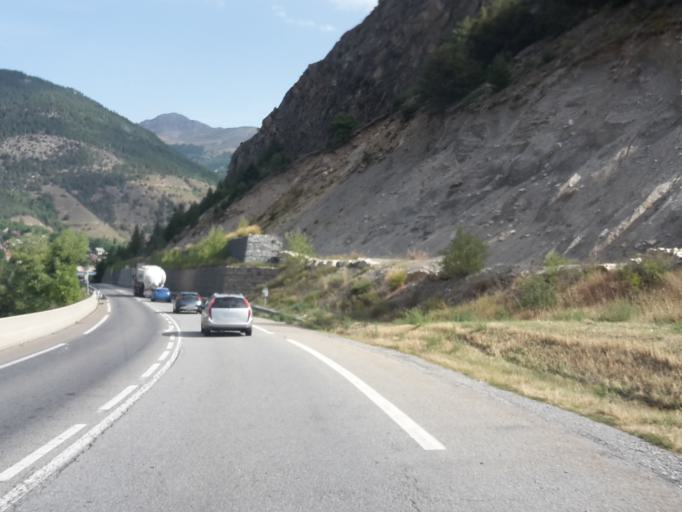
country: FR
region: Provence-Alpes-Cote d'Azur
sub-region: Departement des Hautes-Alpes
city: Saint-Martin-de-Queyrieres
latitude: 44.8458
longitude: 6.5833
